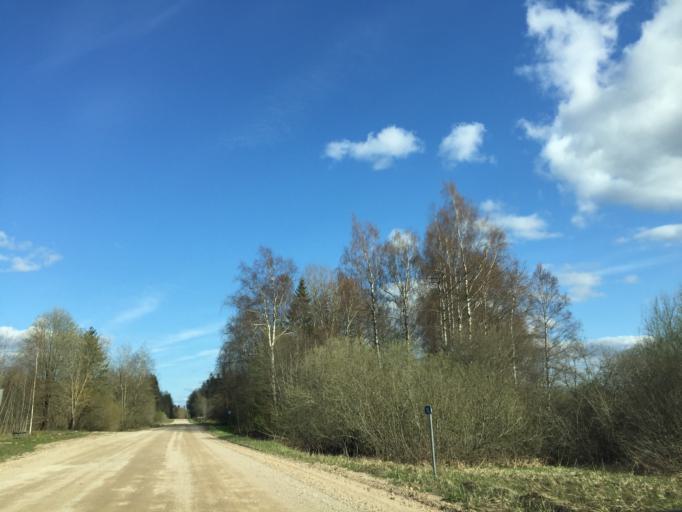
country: LV
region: Rezekne
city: Rezekne
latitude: 56.6472
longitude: 27.3680
